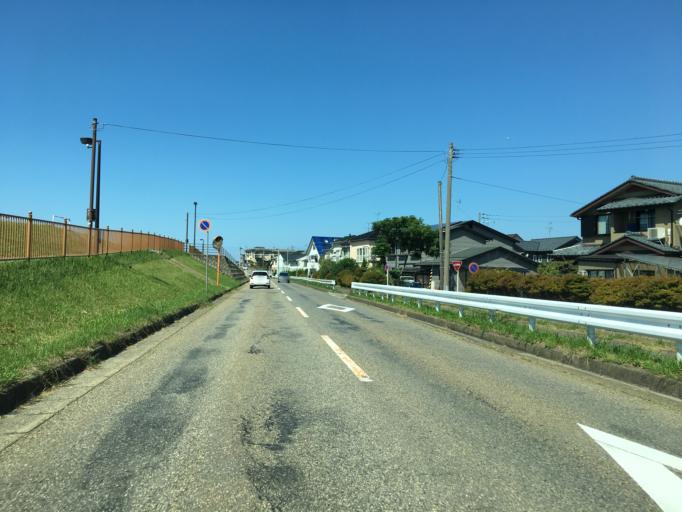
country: JP
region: Niigata
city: Niigata-shi
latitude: 37.8988
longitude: 139.0110
